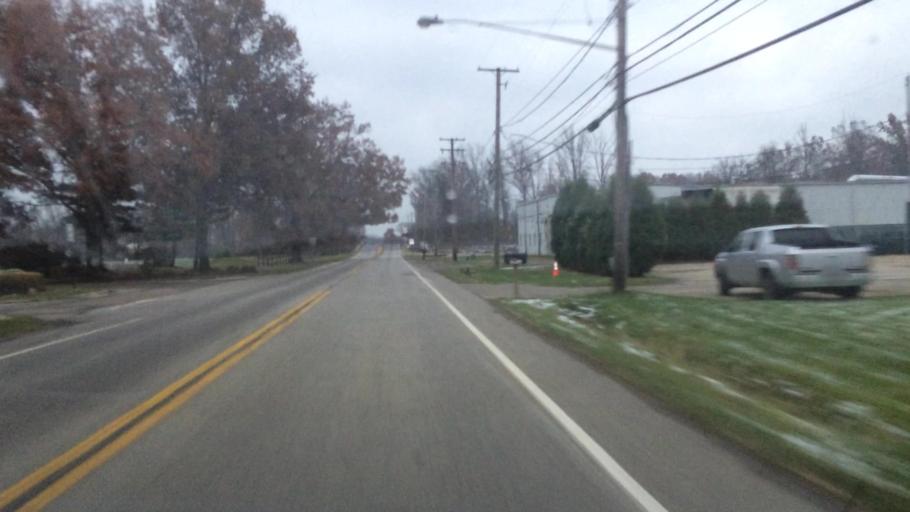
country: US
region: Ohio
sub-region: Cuyahoga County
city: Olmsted Falls
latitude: 41.3508
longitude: -81.9146
